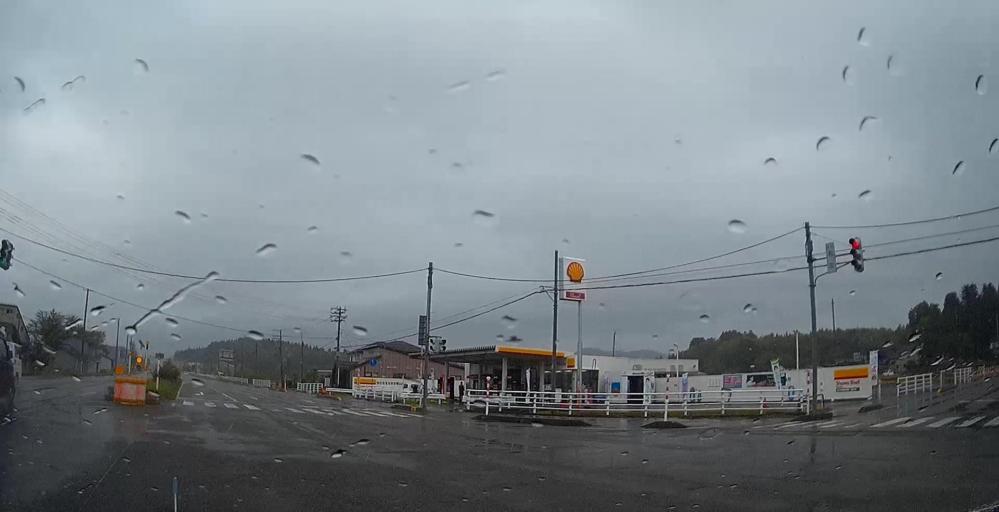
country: JP
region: Niigata
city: Kashiwazaki
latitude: 37.4474
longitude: 138.6411
